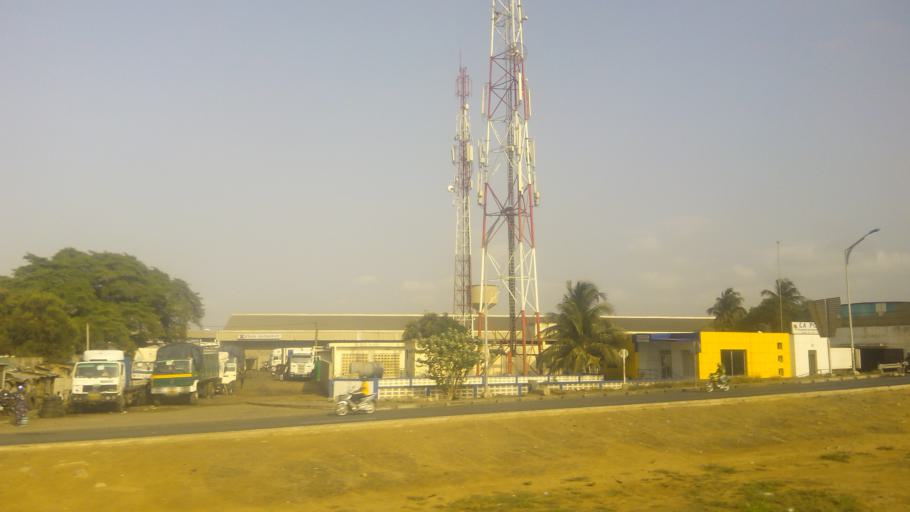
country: TG
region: Maritime
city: Lome
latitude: 6.1435
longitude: 1.2759
